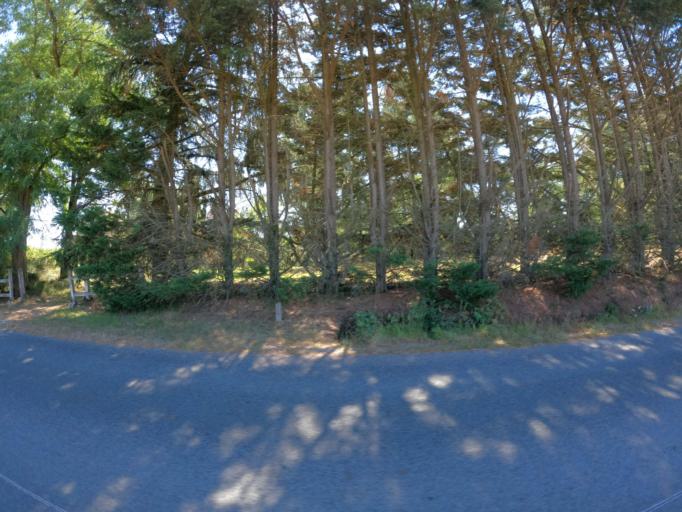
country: FR
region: Pays de la Loire
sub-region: Departement de la Vendee
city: Saint-Philbert-de-Bouaine
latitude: 46.9748
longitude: -1.5483
